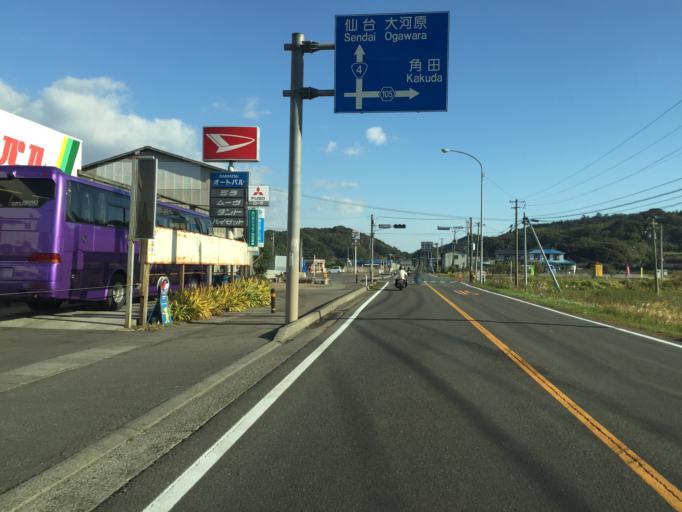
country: JP
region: Miyagi
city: Shiroishi
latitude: 37.9303
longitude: 140.6050
